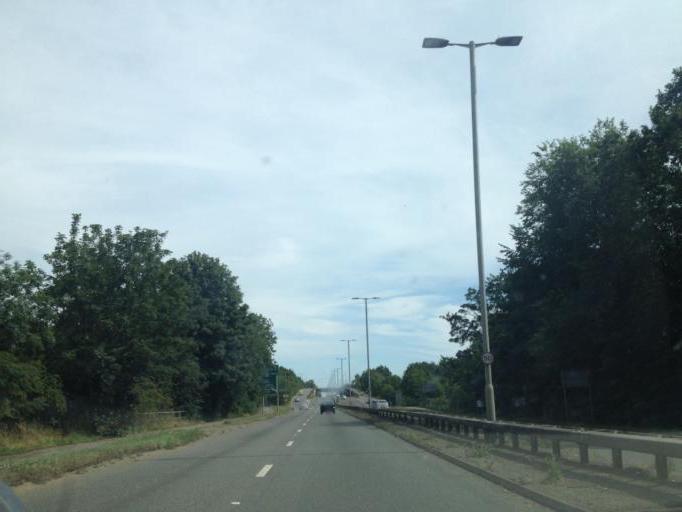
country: GB
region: England
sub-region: Hertfordshire
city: Watford
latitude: 51.6746
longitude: -0.3763
